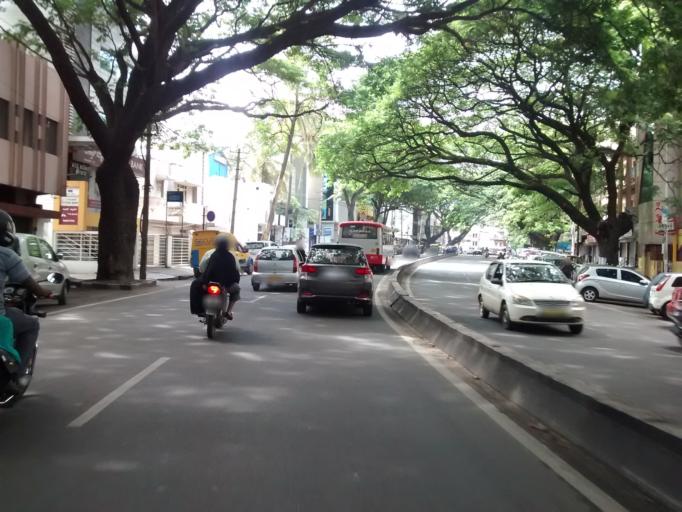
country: IN
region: Karnataka
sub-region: Bangalore Urban
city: Bangalore
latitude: 12.9991
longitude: 77.5526
